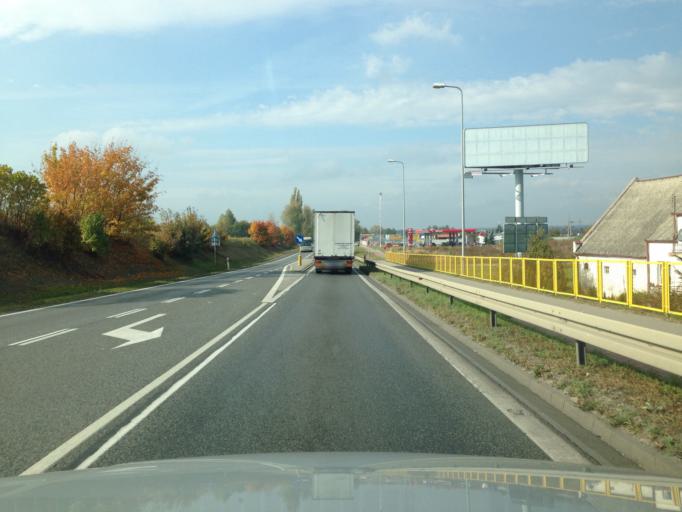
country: PL
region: Kujawsko-Pomorskie
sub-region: Grudziadz
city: Grudziadz
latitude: 53.4878
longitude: 18.7253
